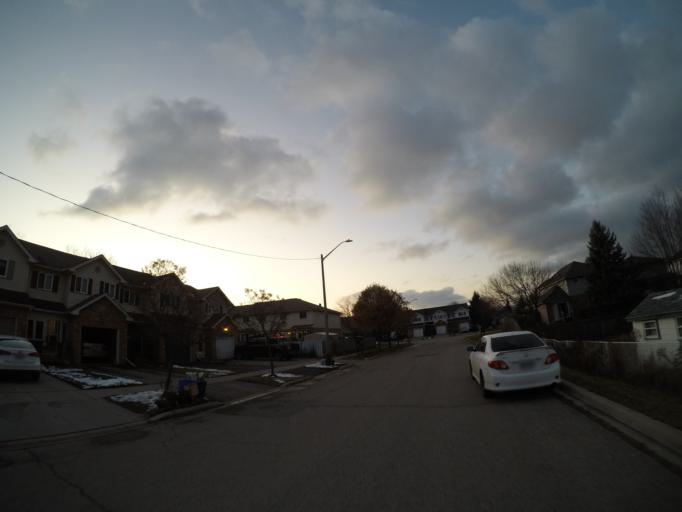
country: CA
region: Ontario
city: Waterloo
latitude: 43.4875
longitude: -80.4834
